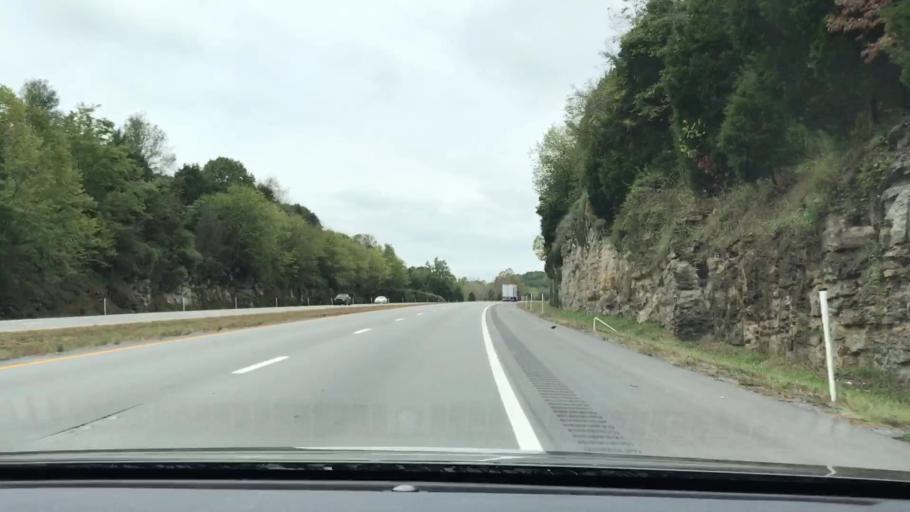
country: US
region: Kentucky
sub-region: Adair County
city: Columbia
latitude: 37.0422
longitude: -85.4518
